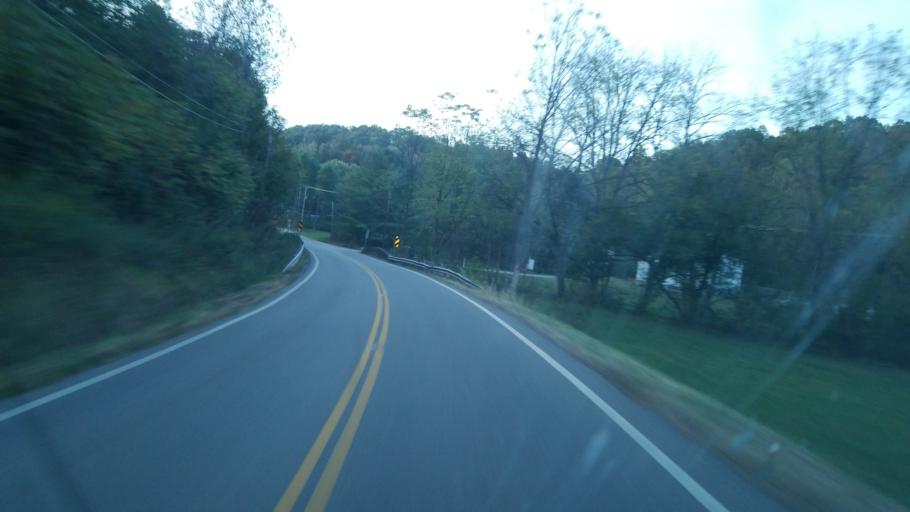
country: US
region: Ohio
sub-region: Meigs County
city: Pomeroy
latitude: 39.0588
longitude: -82.0594
